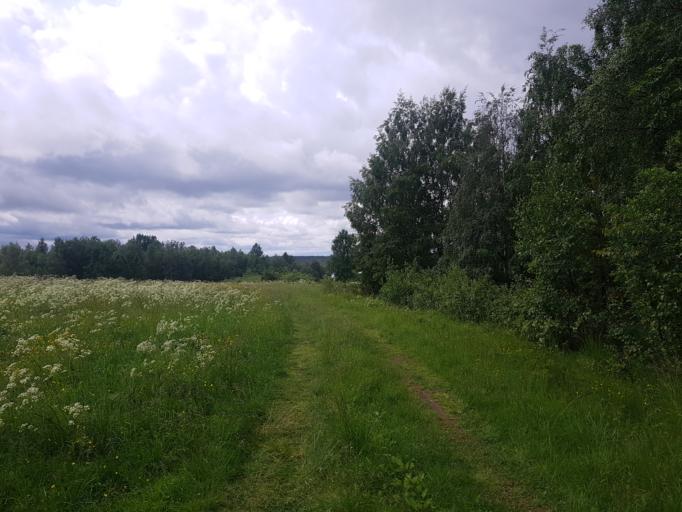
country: RU
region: Republic of Karelia
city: Kostomuksha
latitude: 64.8329
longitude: 29.8875
